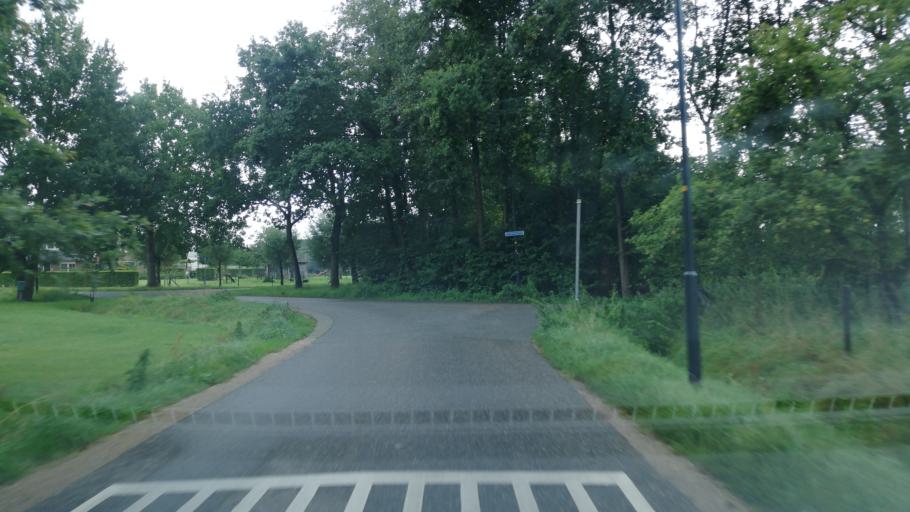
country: NL
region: Gelderland
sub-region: Gemeente Epe
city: Vaassen
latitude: 52.2660
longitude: 5.9897
